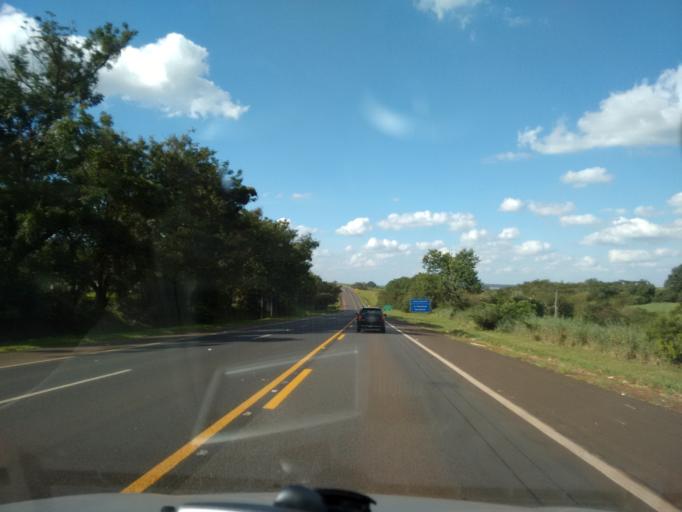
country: BR
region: Sao Paulo
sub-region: Americo Brasiliense
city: Americo Brasiliense
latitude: -21.7592
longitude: -48.0745
